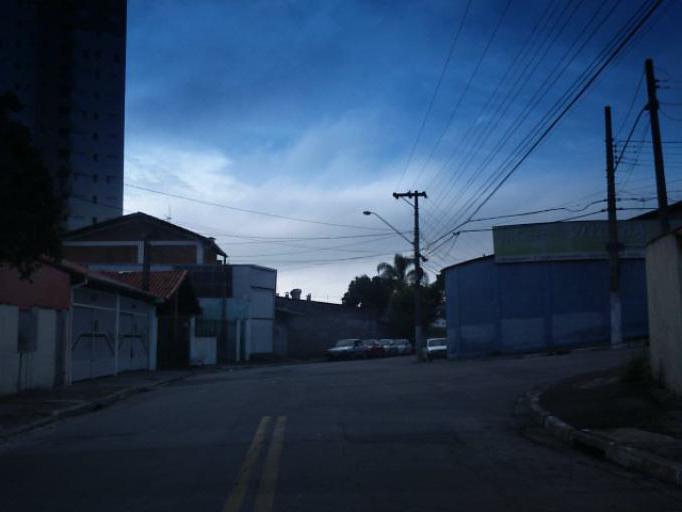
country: BR
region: Sao Paulo
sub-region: Sao Jose Dos Campos
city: Sao Jose dos Campos
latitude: -23.2006
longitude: -45.8624
